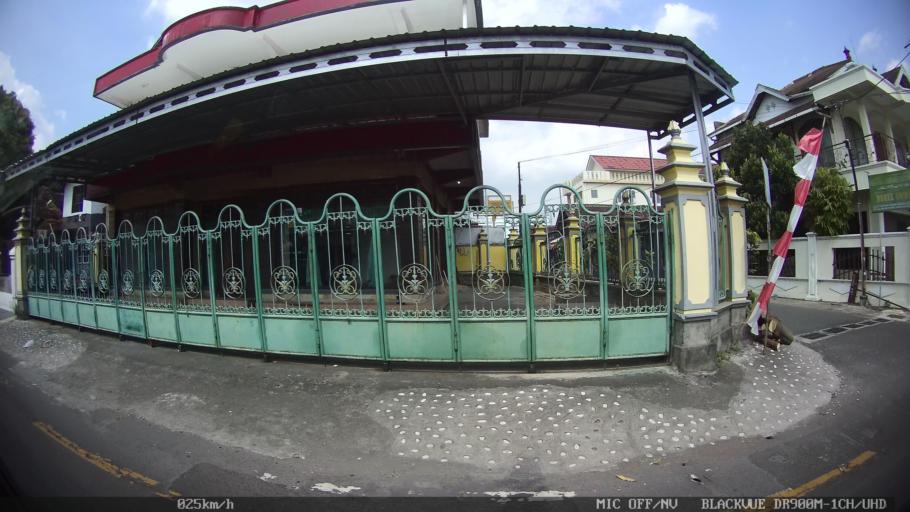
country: ID
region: Daerah Istimewa Yogyakarta
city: Yogyakarta
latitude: -7.8256
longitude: 110.3949
